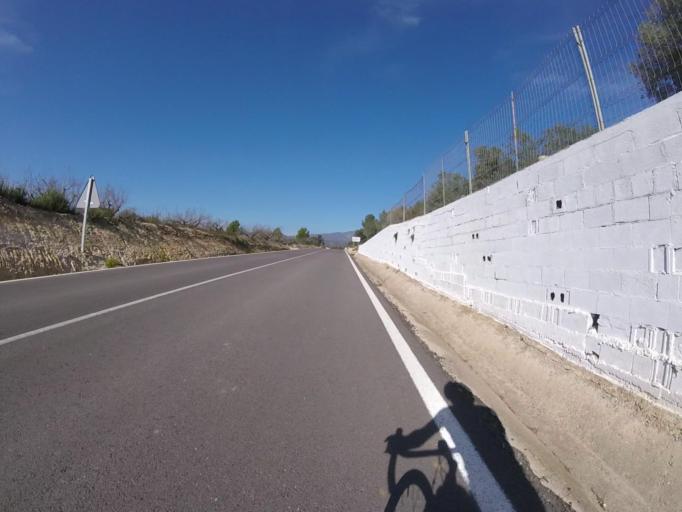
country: ES
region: Valencia
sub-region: Provincia de Castello
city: Cuevas de Vinroma
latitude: 40.2597
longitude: 0.0797
